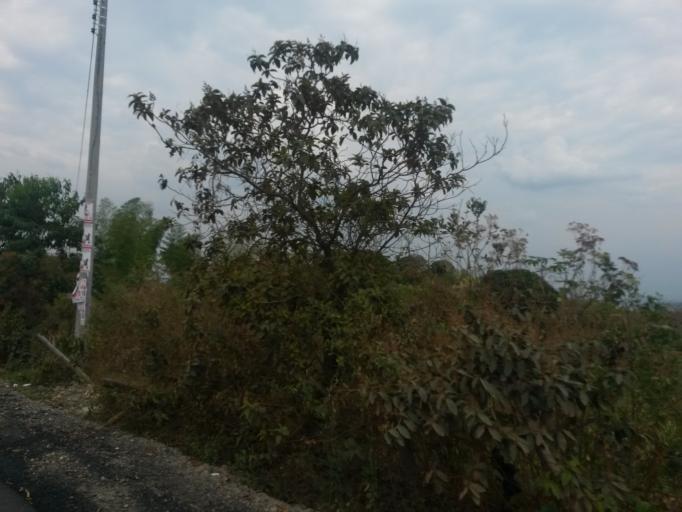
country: CO
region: Cauca
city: Buenos Aires
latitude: 3.0529
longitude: -76.6345
